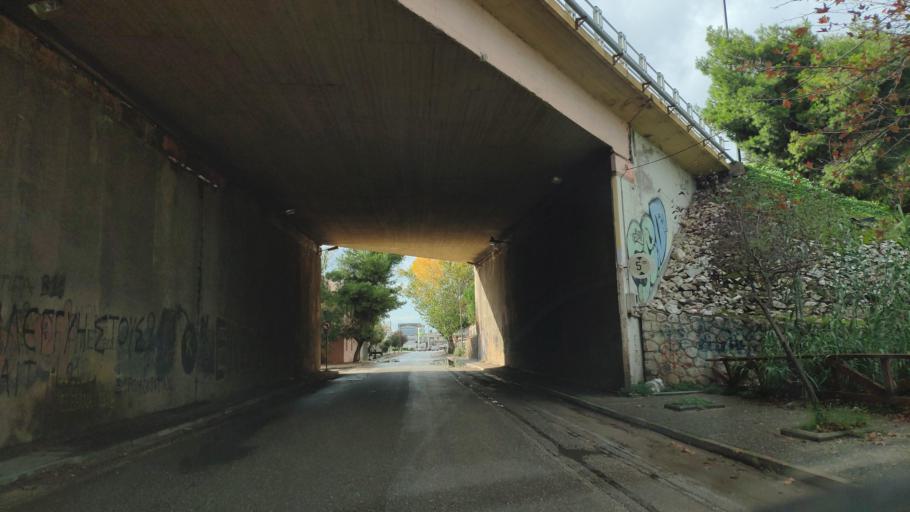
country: GR
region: Attica
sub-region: Nomarchia Dytikis Attikis
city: Elefsina
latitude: 38.0471
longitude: 23.5506
